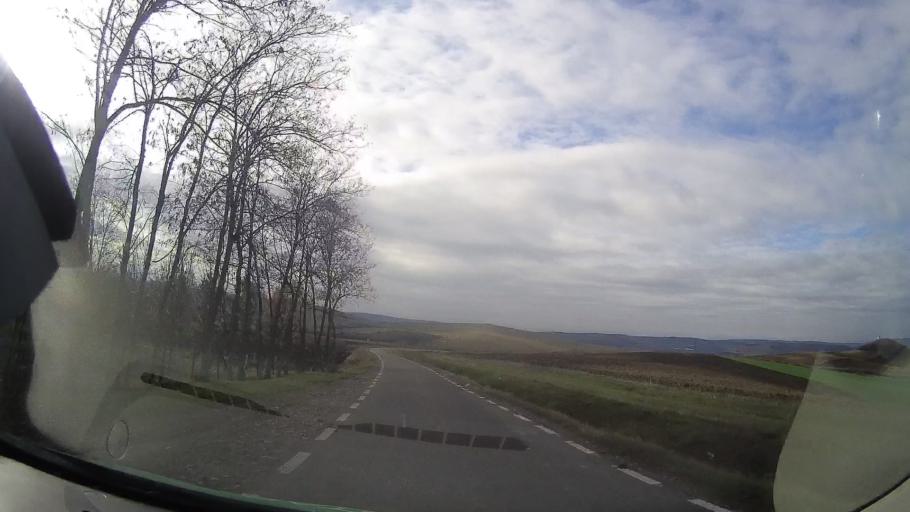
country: RO
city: Barza
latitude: 46.5462
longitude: 24.1505
